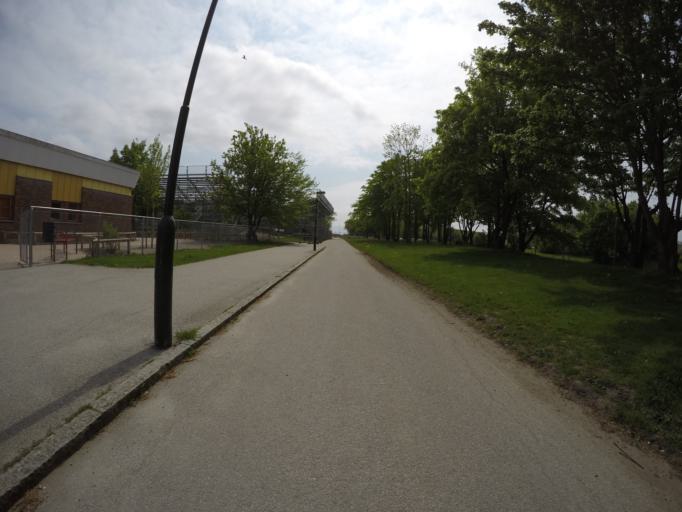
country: SE
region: Skane
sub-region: Malmo
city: Malmoe
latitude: 55.5725
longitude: 12.9759
